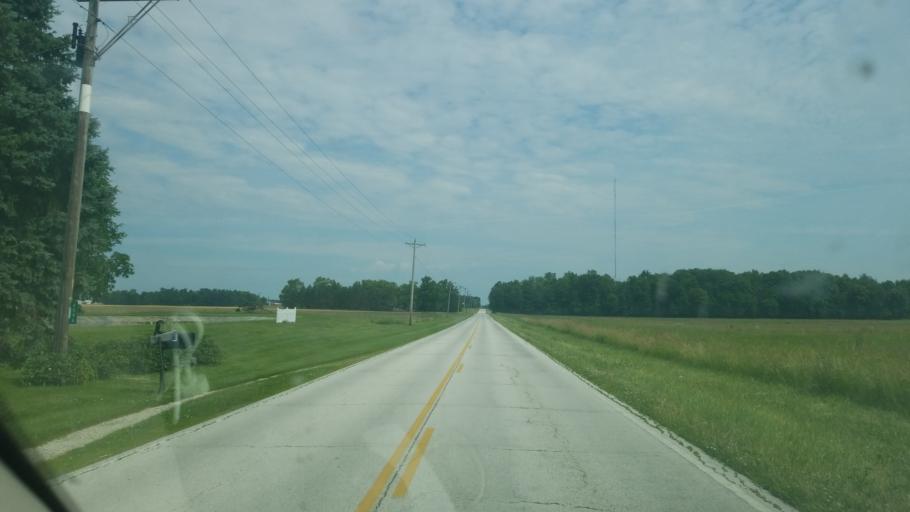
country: US
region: Ohio
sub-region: Seneca County
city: Fostoria
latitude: 41.0964
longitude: -83.4784
